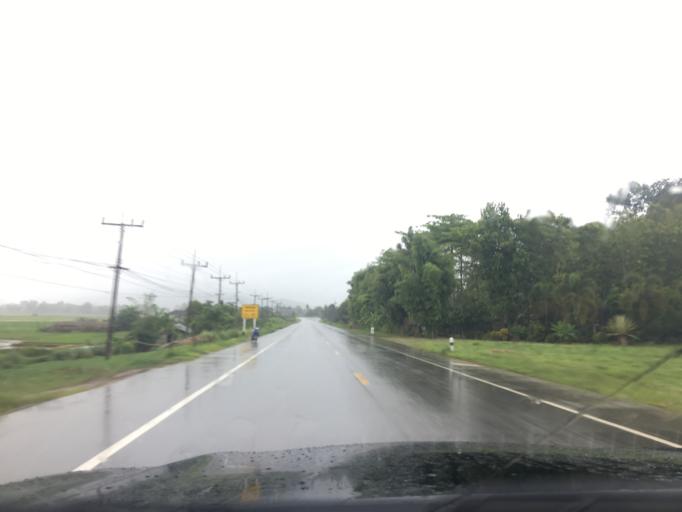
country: TH
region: Chiang Rai
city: Chiang Saen
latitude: 20.2831
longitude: 100.2153
